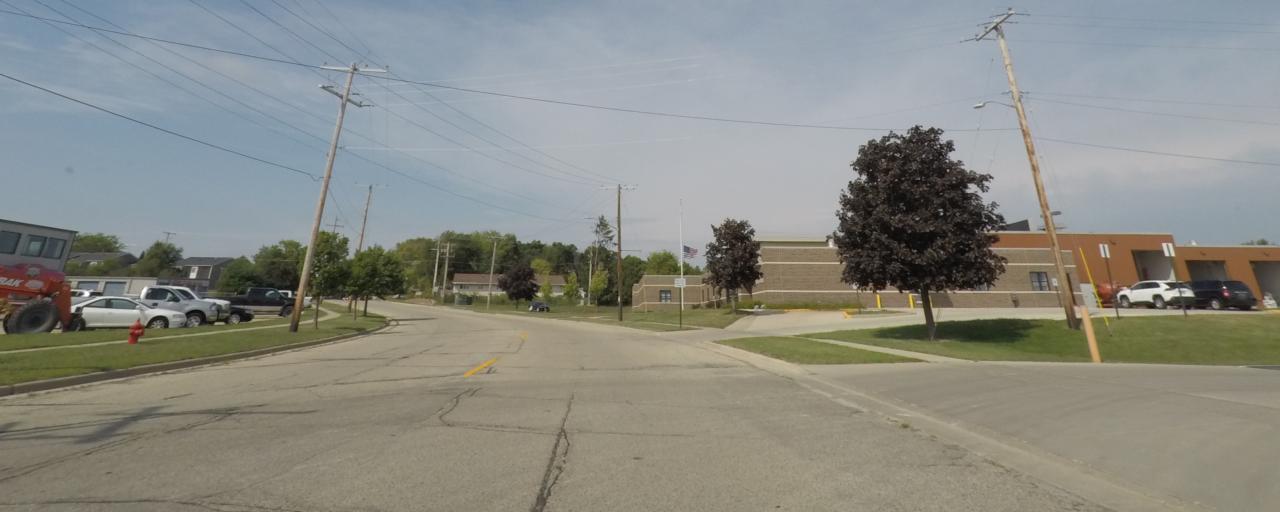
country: US
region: Wisconsin
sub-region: Jefferson County
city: Jefferson
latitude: 42.9909
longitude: -88.8151
